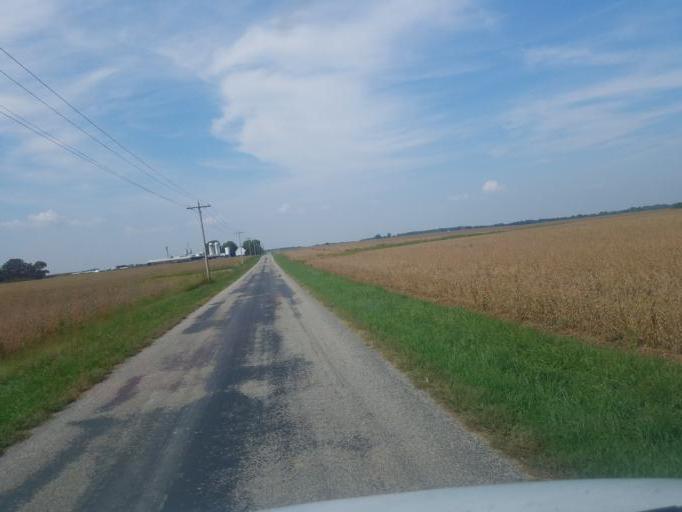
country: US
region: Ohio
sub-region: Marion County
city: Marion
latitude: 40.6587
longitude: -83.2708
